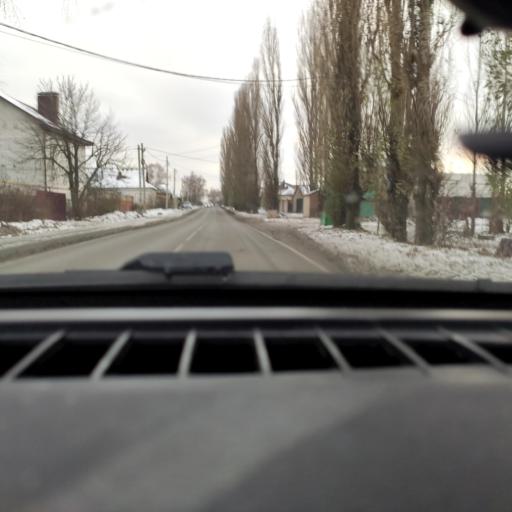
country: RU
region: Voronezj
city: Podgornoye
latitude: 51.8011
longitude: 39.1431
